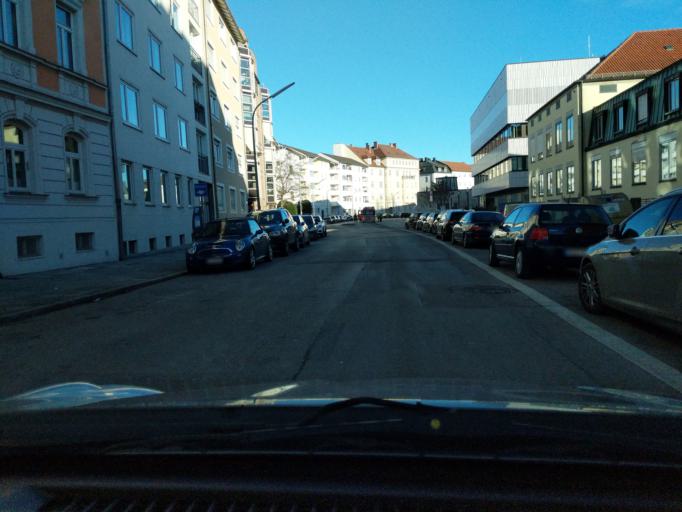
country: DE
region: Bavaria
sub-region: Upper Bavaria
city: Munich
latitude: 48.1509
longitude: 11.5850
